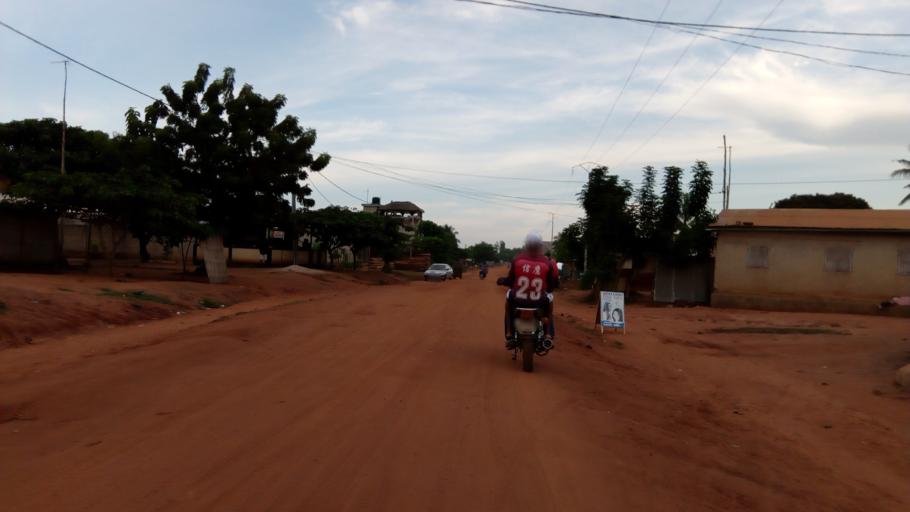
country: TG
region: Maritime
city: Lome
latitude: 6.2607
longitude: 1.1389
